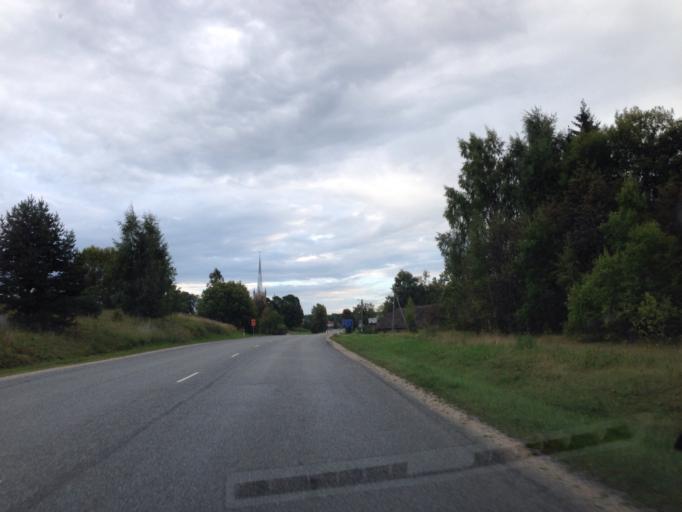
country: EE
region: Tartu
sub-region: Elva linn
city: Elva
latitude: 58.1454
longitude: 26.2393
